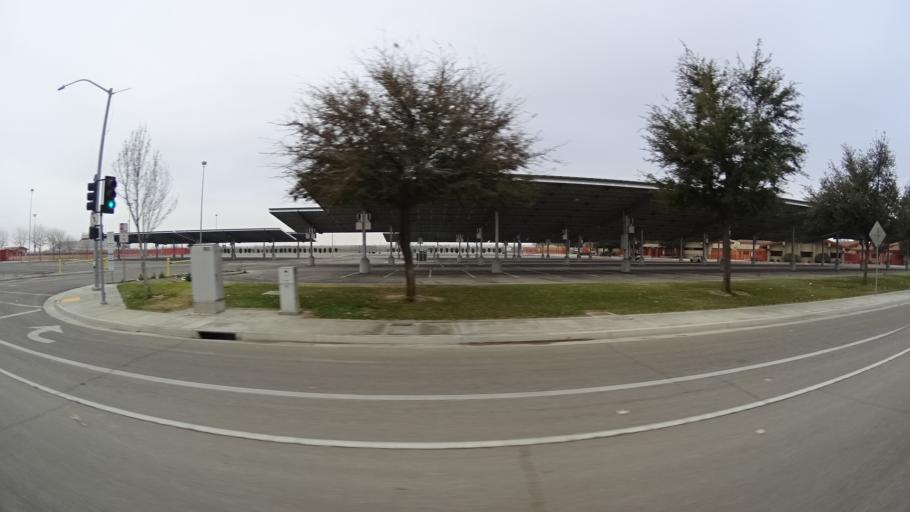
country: US
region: California
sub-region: Kern County
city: Lamont
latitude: 35.3367
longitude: -118.9321
